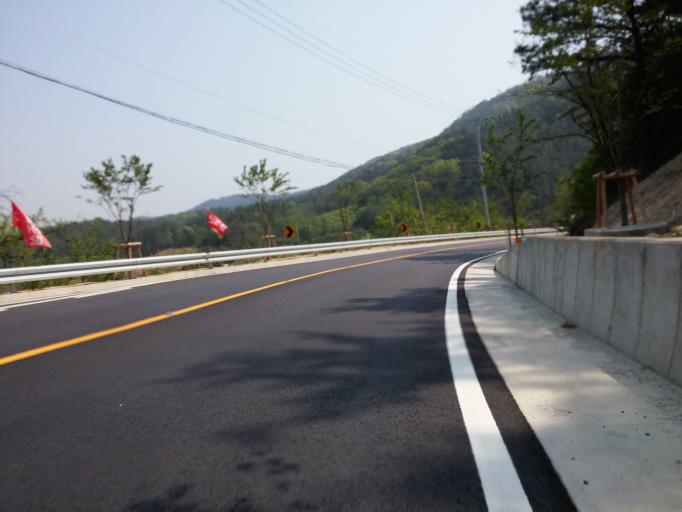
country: KR
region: Chungcheongbuk-do
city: Okcheon
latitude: 36.3746
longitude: 127.5108
